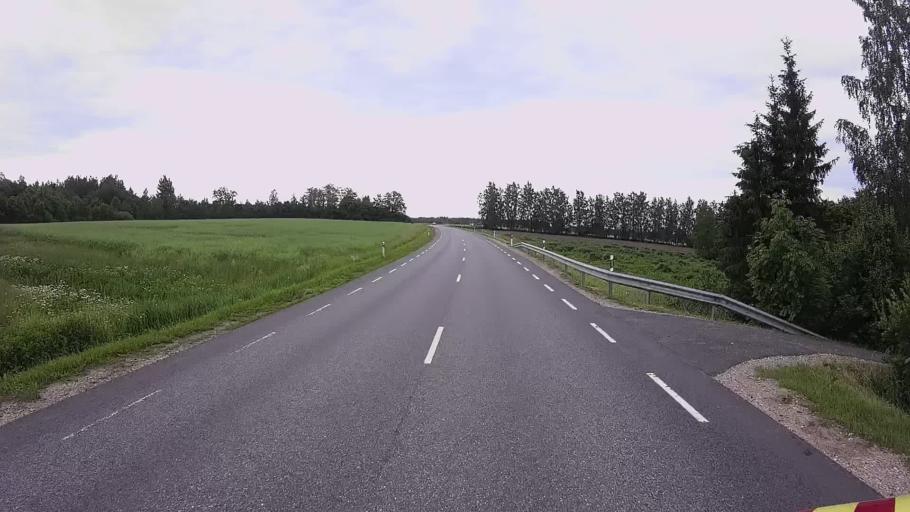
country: EE
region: Viljandimaa
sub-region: Karksi vald
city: Karksi-Nuia
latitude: 58.1617
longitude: 25.5883
